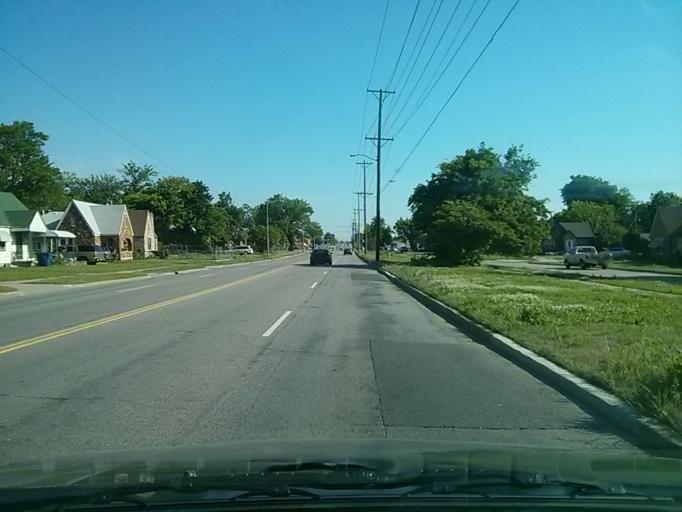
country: US
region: Oklahoma
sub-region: Tulsa County
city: Tulsa
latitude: 36.1881
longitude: -95.9934
